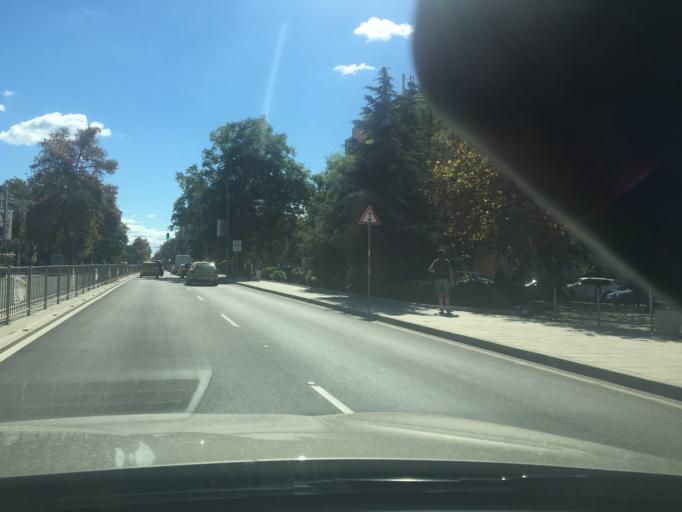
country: BG
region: Burgas
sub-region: Obshtina Burgas
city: Burgas
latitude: 42.5077
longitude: 27.4684
